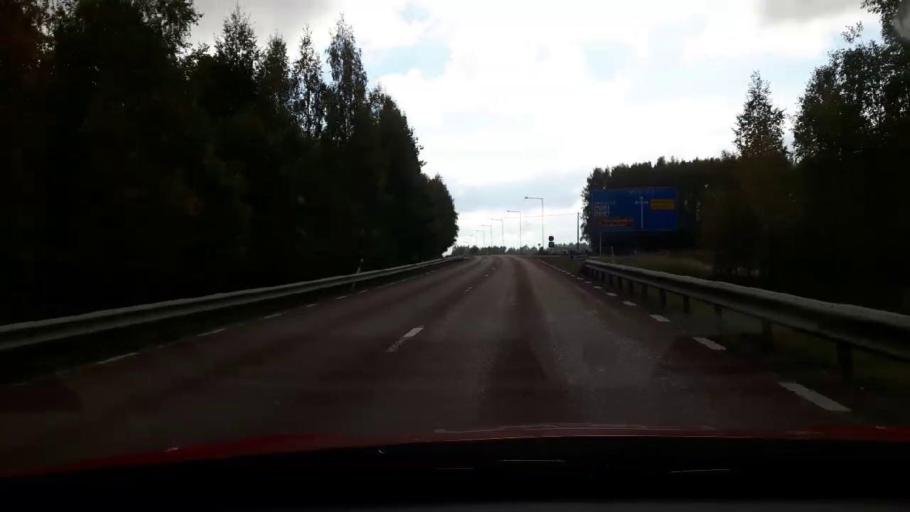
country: SE
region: Gaevleborg
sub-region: Bollnas Kommun
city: Arbra
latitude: 61.5455
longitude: 16.3534
